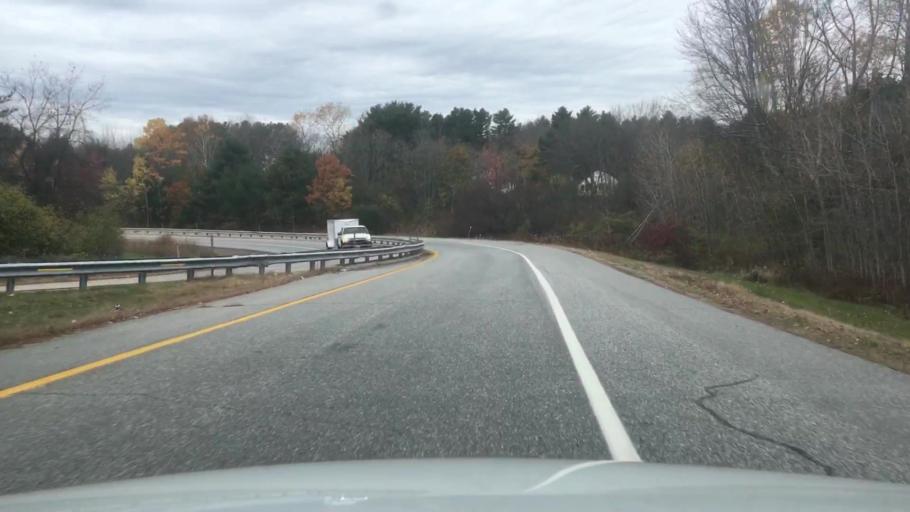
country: US
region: Maine
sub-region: Cumberland County
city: Falmouth
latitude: 43.7298
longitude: -70.2355
